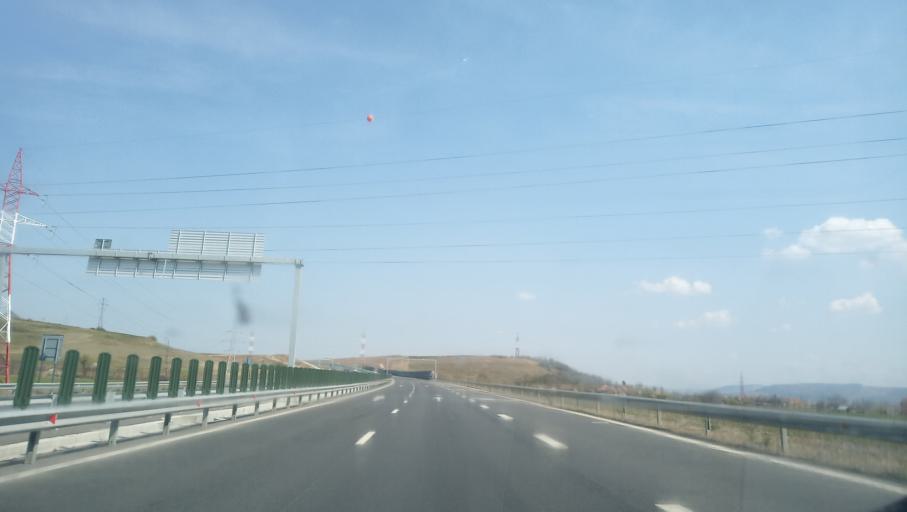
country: RO
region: Alba
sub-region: Comuna Unirea
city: Unirea
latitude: 46.3886
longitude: 23.7756
